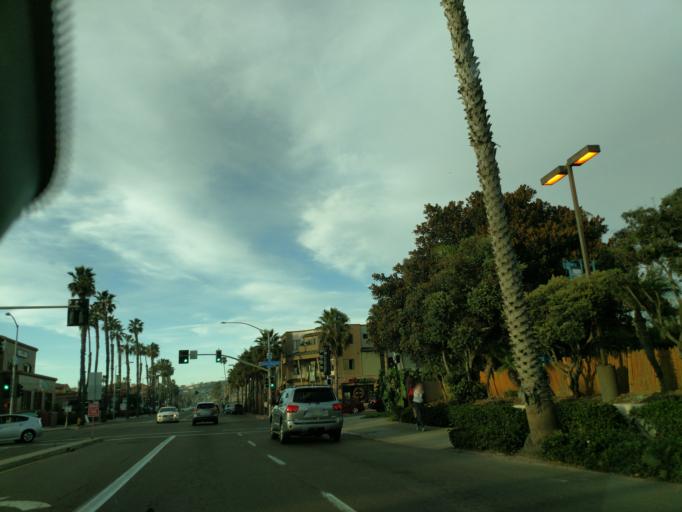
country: US
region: California
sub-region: San Diego County
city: La Jolla
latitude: 32.7905
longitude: -117.2536
